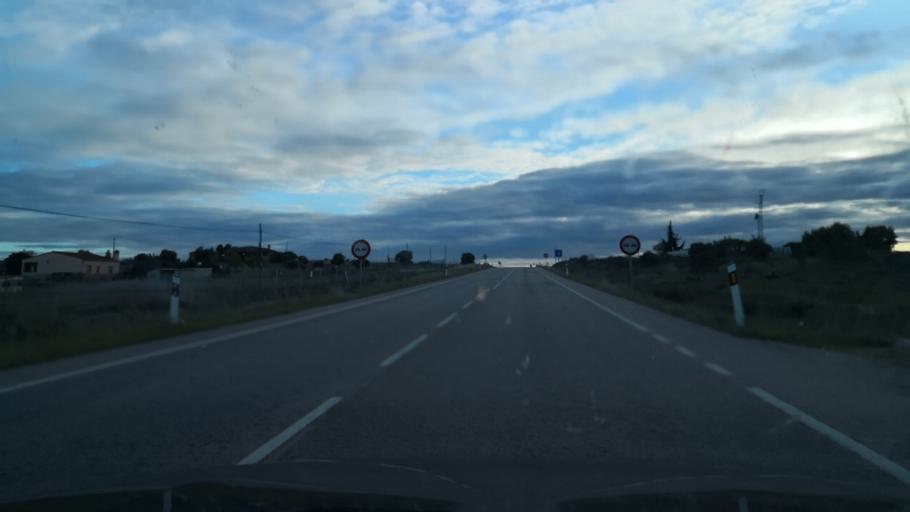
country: ES
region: Extremadura
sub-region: Provincia de Caceres
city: Malpartida de Caceres
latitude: 39.3836
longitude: -6.4419
